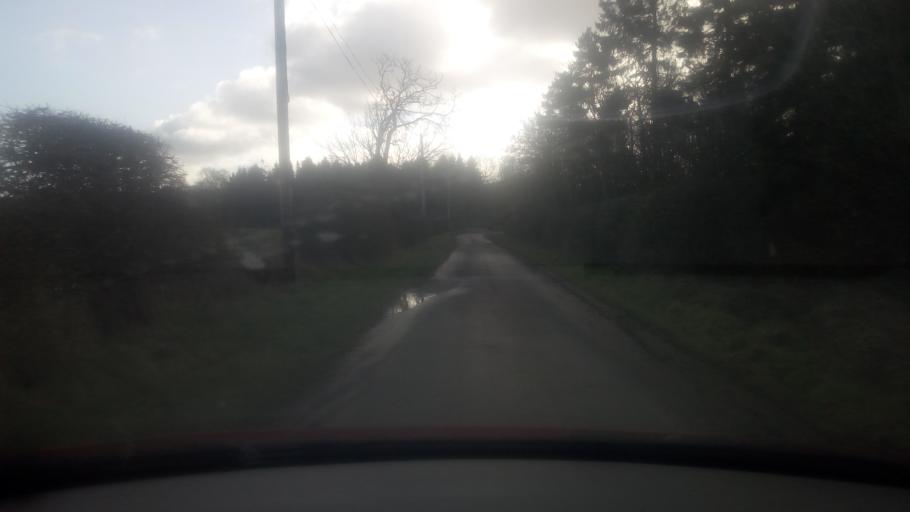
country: GB
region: Scotland
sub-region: The Scottish Borders
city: Saint Boswells
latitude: 55.5215
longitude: -2.6531
